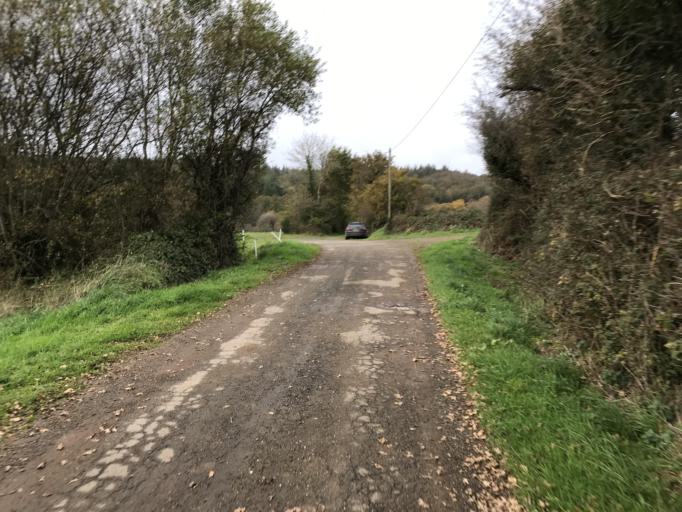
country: FR
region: Brittany
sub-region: Departement du Finistere
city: Hopital-Camfrout
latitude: 48.3245
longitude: -4.2145
